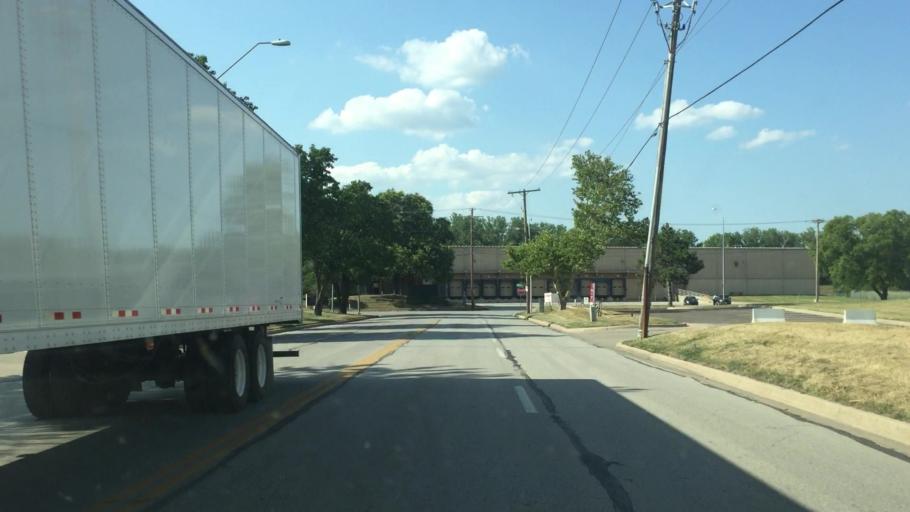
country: US
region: Missouri
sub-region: Clay County
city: North Kansas City
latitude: 39.1428
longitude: -94.5136
